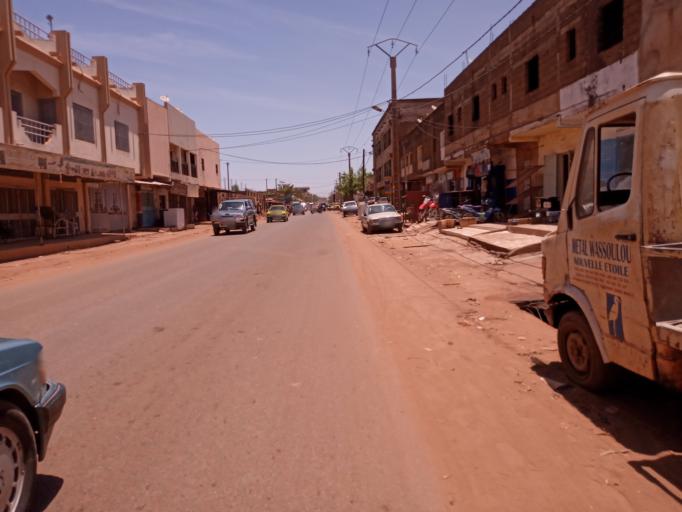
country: ML
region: Bamako
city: Bamako
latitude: 12.5883
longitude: -7.9743
